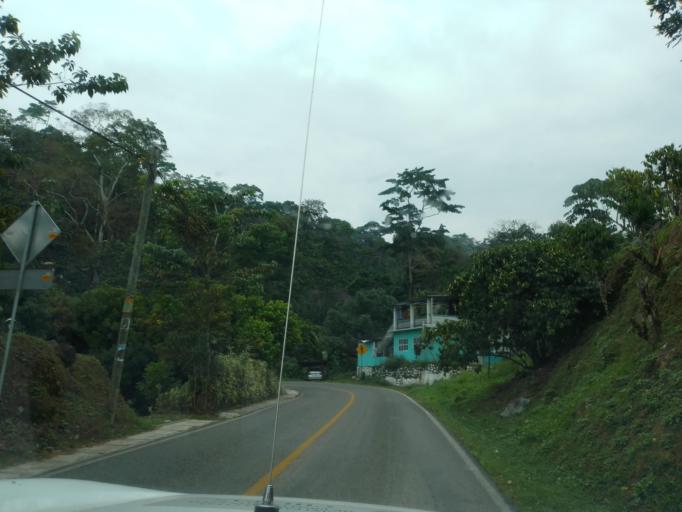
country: MX
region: Chiapas
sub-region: Union Juarez
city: Santo Domingo
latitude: 15.0380
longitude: -92.1175
